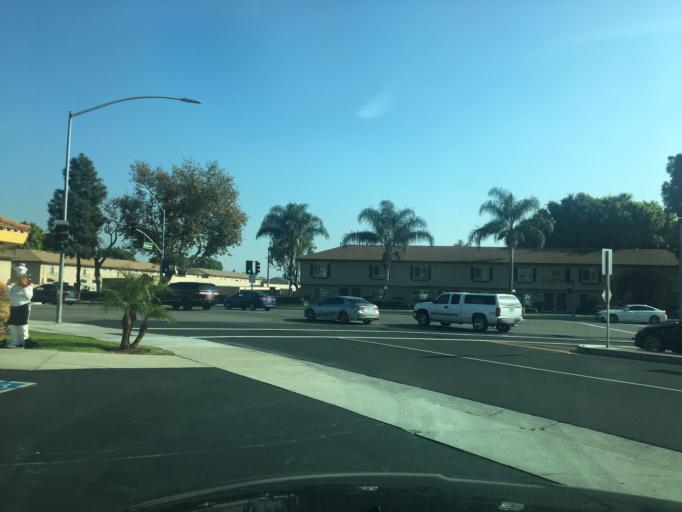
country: US
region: California
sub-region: Orange County
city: Tustin
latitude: 33.7341
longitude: -117.8268
